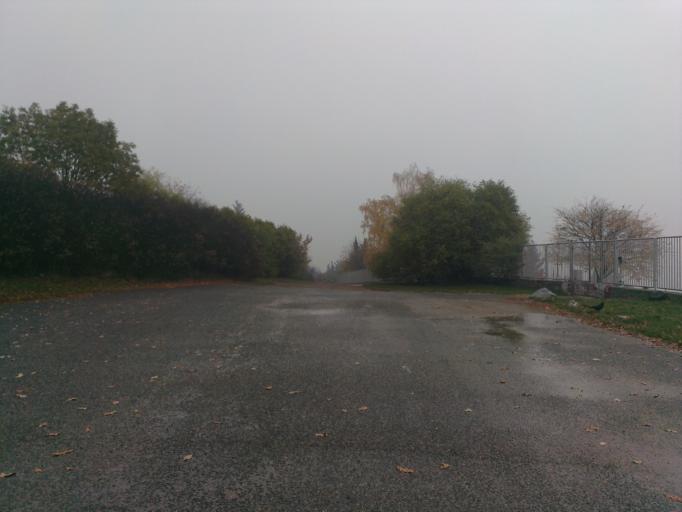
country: CZ
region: South Moravian
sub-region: Mesto Brno
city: Brno
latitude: 49.2014
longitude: 16.5872
